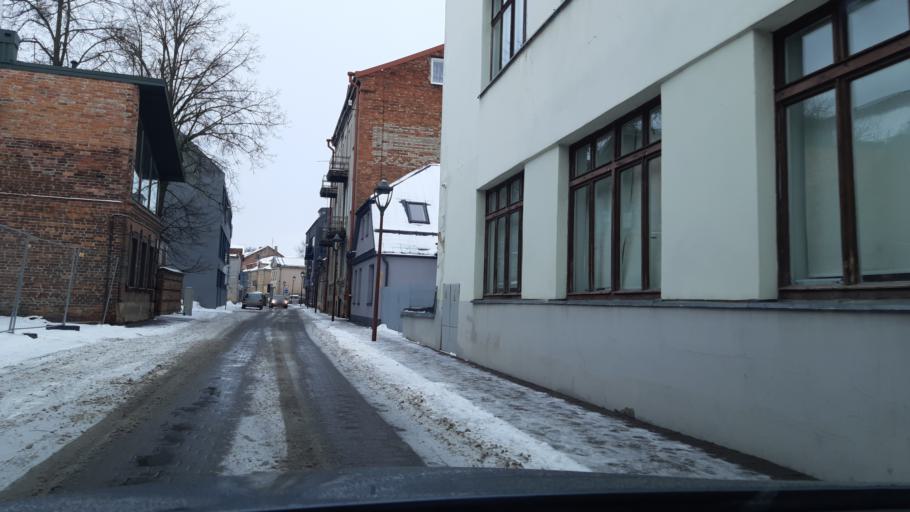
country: LT
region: Kauno apskritis
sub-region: Kaunas
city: Kaunas
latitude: 54.8952
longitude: 23.8981
